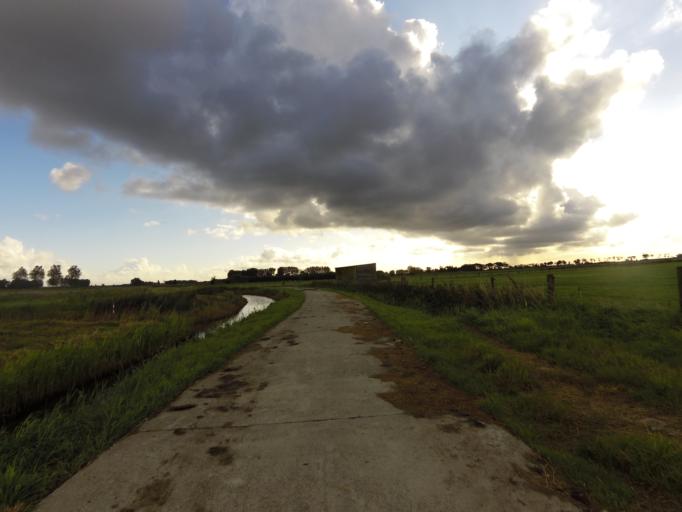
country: BE
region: Flanders
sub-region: Provincie West-Vlaanderen
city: Middelkerke
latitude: 51.1738
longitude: 2.8506
